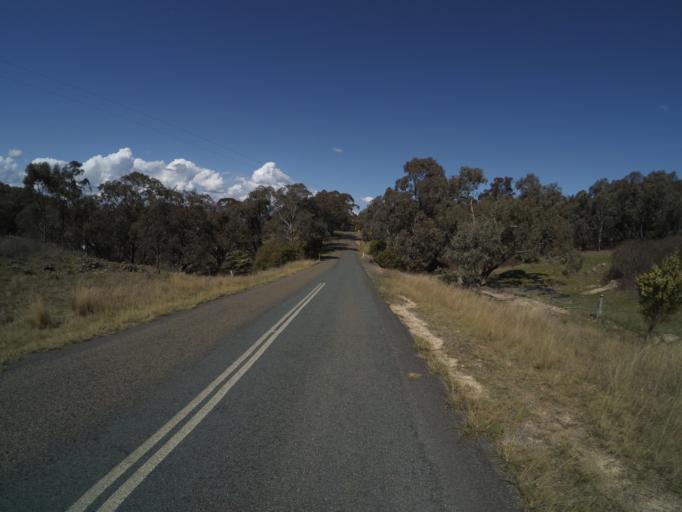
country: AU
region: Australian Capital Territory
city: Macquarie
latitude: -35.2032
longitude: 148.8983
